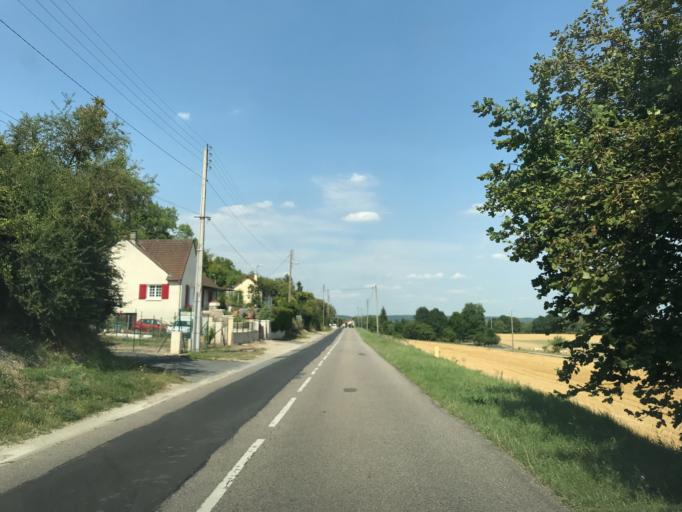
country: FR
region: Ile-de-France
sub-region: Departement des Yvelines
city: Bonnieres-sur-Seine
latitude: 49.0477
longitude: 1.5839
